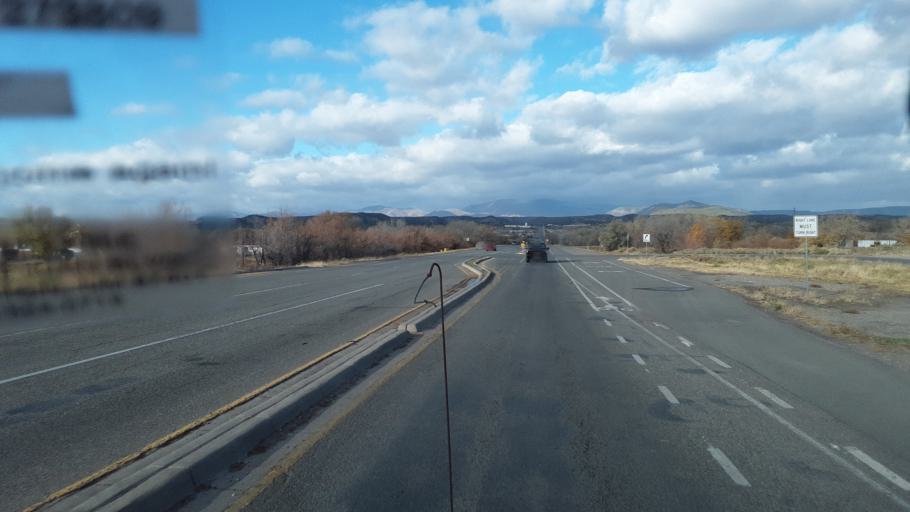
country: US
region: New Mexico
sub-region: Rio Arriba County
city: Espanola
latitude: 36.0082
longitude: -106.0665
